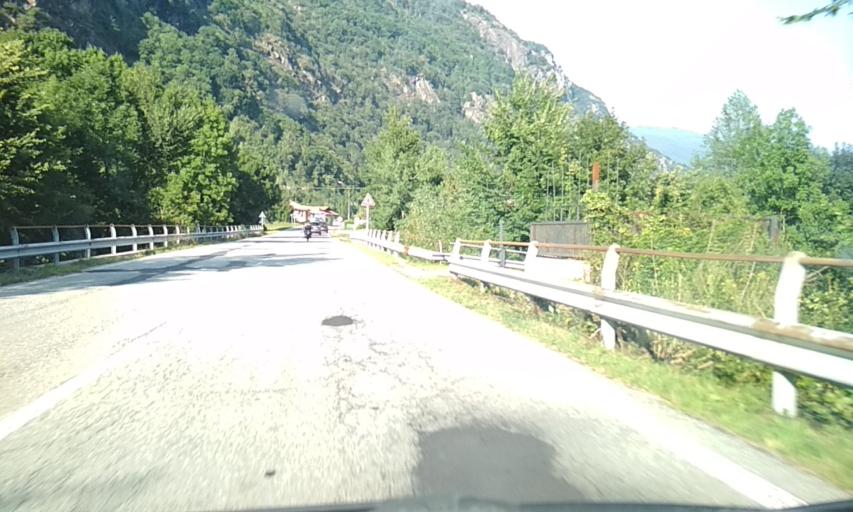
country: IT
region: Piedmont
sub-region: Provincia di Torino
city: Sparone
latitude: 45.4168
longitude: 7.5586
